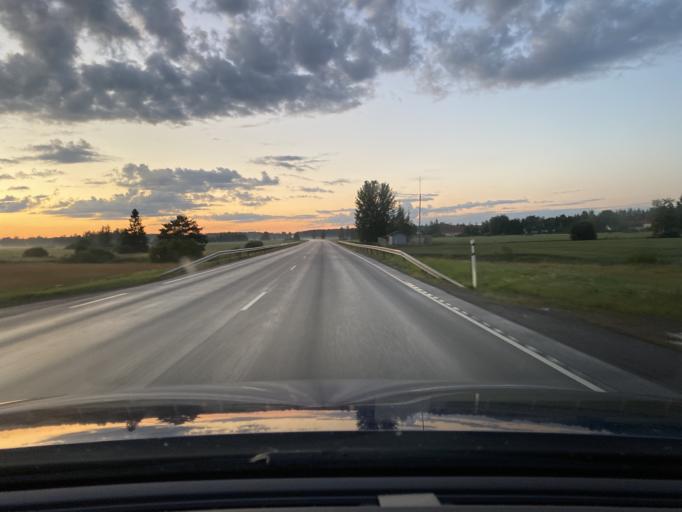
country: FI
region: Varsinais-Suomi
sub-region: Loimaa
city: Aura
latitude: 60.6735
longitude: 22.5633
